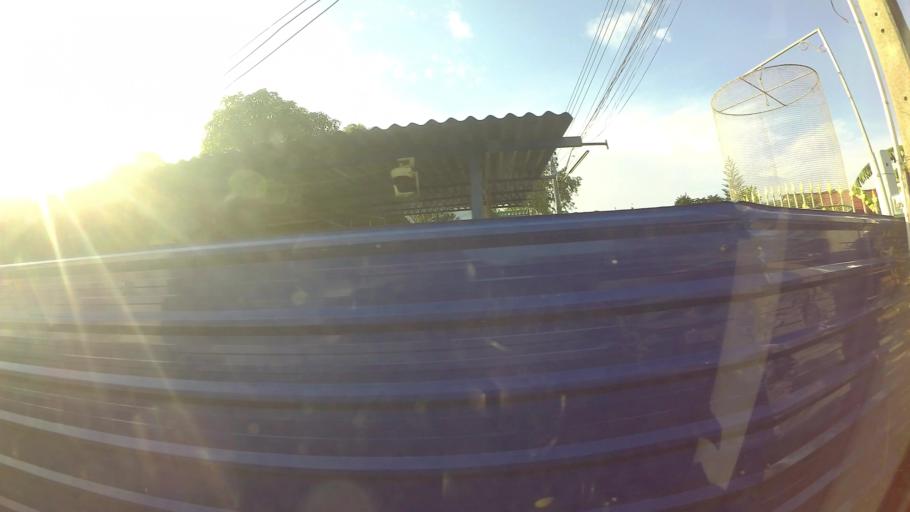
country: TH
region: Rayong
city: Rayong
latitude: 12.6861
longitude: 101.2891
